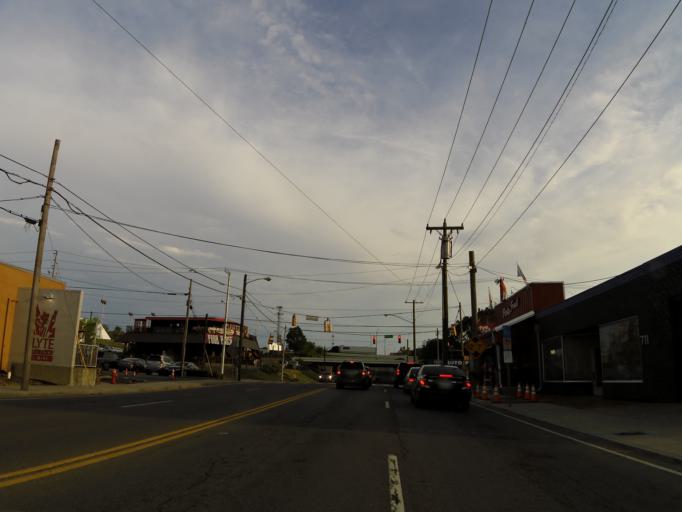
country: US
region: Tennessee
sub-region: Davidson County
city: Nashville
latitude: 36.1502
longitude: -86.7793
